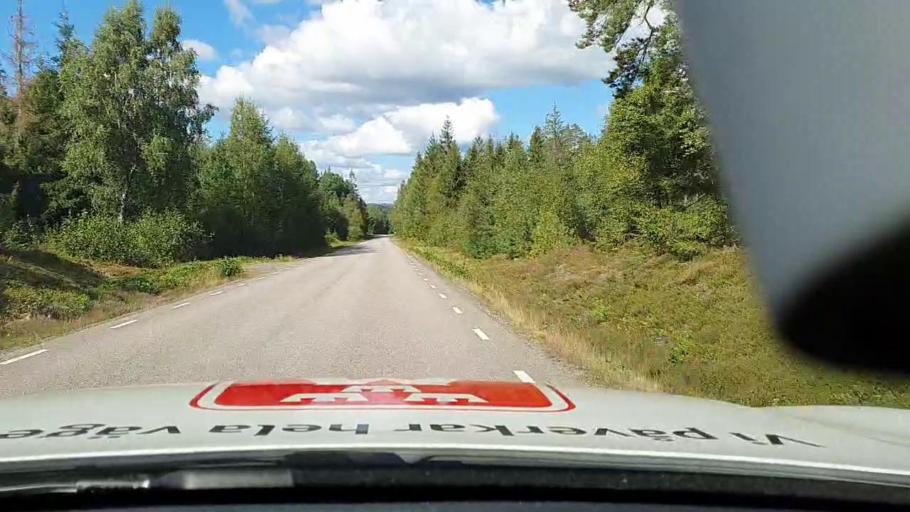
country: SE
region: Vaestra Goetaland
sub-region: Marks Kommun
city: Fritsla
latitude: 57.3903
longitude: 12.8539
